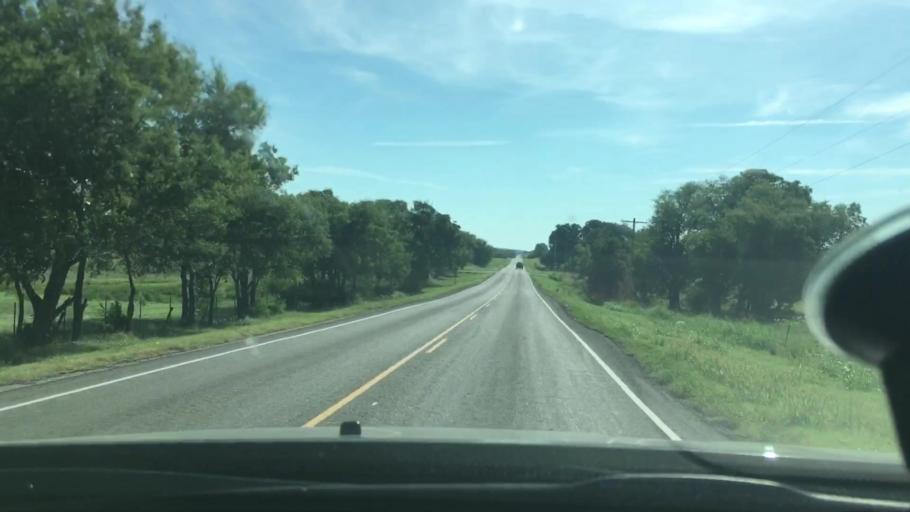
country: US
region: Oklahoma
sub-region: Carter County
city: Ardmore
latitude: 34.3327
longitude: -97.1803
